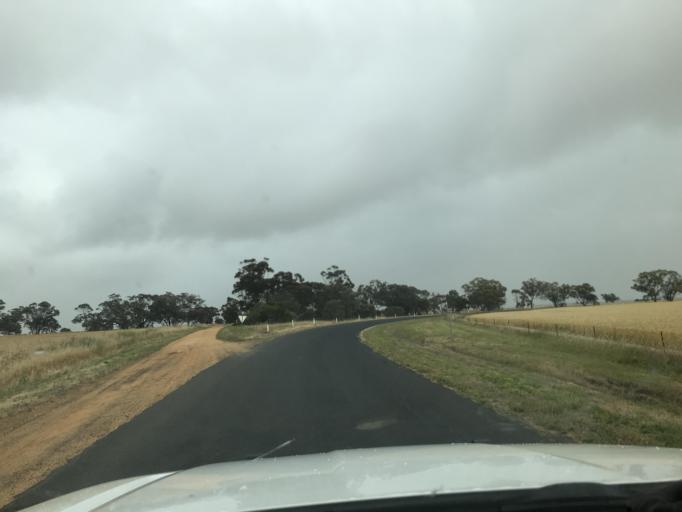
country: AU
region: South Australia
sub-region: Tatiara
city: Bordertown
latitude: -36.3429
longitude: 141.2175
